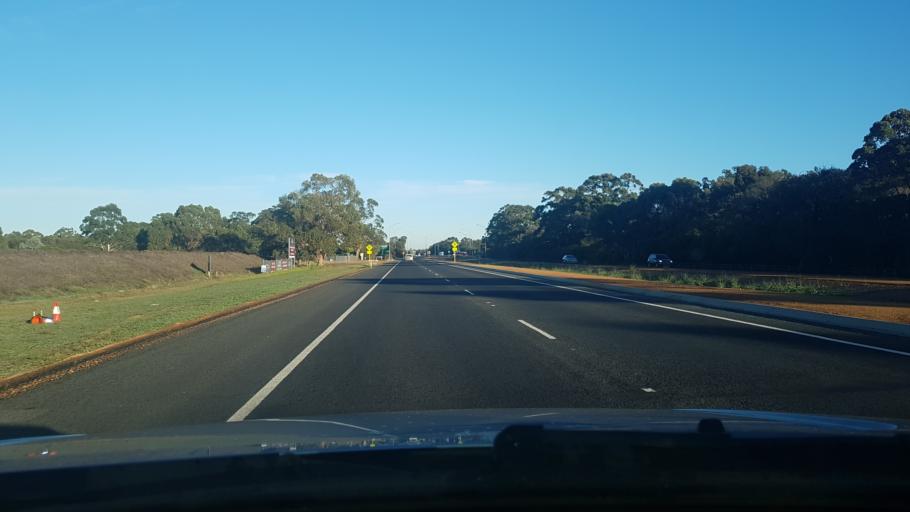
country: AU
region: Western Australia
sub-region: Busselton
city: Busselton
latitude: -33.6711
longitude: 115.3216
